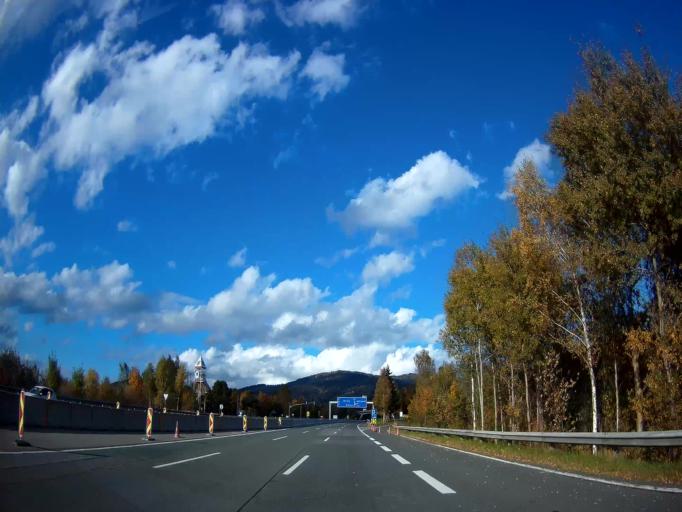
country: AT
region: Carinthia
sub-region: Politischer Bezirk Wolfsberg
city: Bad Sankt Leonhard im Lavanttal
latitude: 46.9268
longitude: 14.8419
